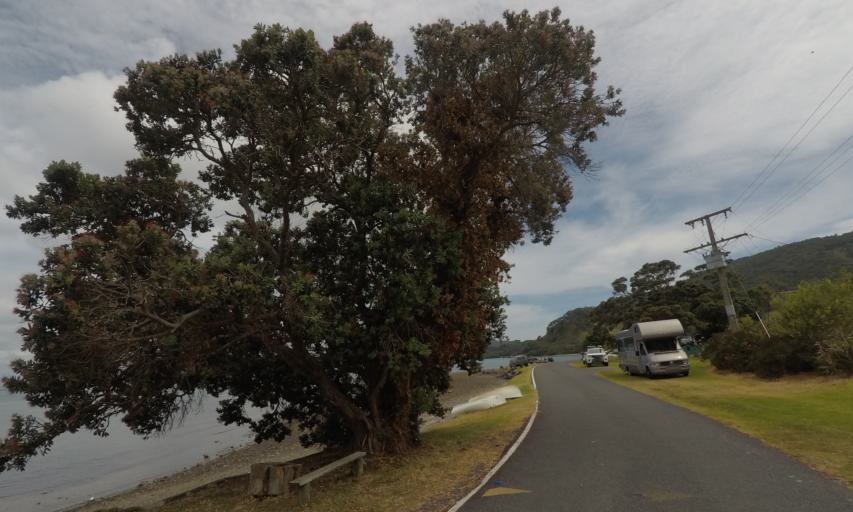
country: NZ
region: Northland
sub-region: Whangarei
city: Ruakaka
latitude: -35.8470
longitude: 174.5354
